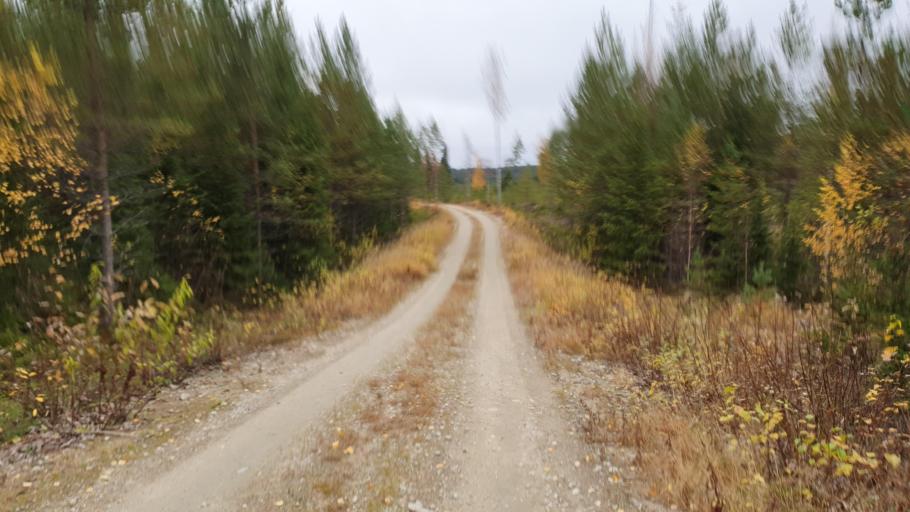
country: FI
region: Kainuu
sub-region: Kehys-Kainuu
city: Kuhmo
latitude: 64.4495
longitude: 29.6119
